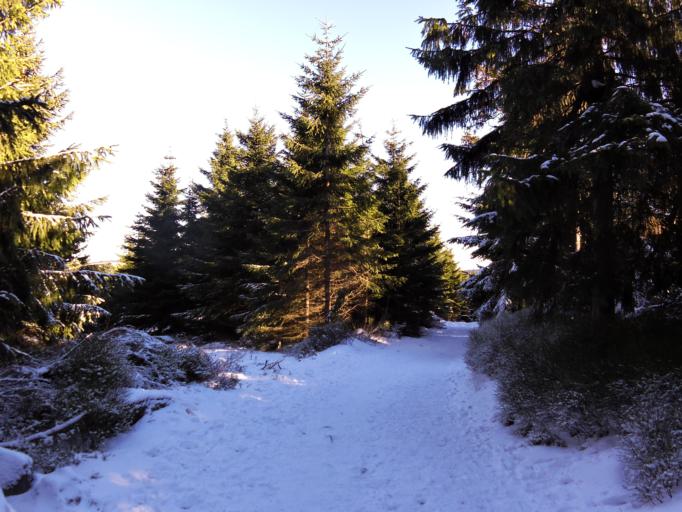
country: DE
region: Bavaria
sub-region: Upper Franconia
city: Bischofsgrun
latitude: 50.0304
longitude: 11.8119
